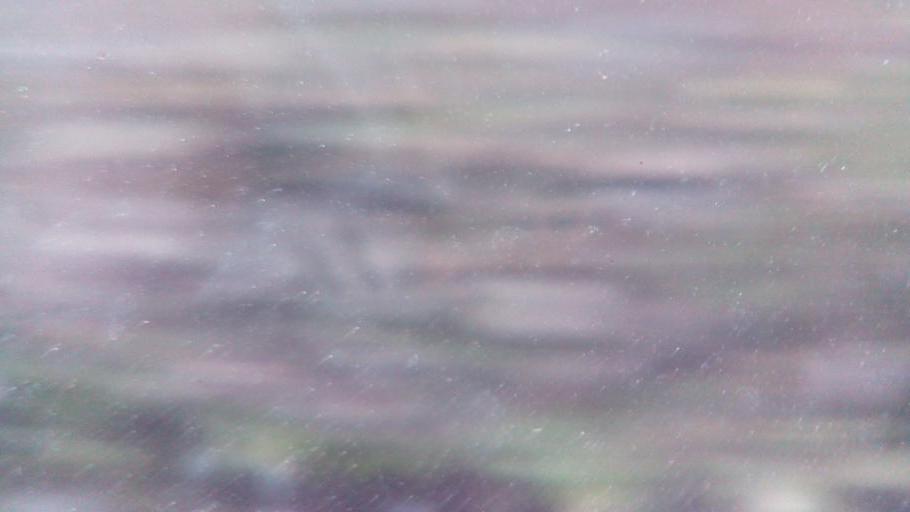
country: TW
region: Taiwan
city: Daxi
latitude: 24.4623
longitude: 121.3943
